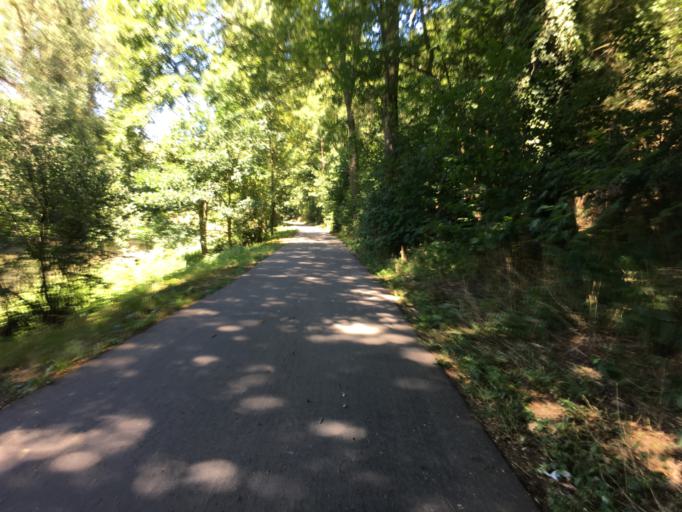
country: DE
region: Baden-Wuerttemberg
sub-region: Karlsruhe Region
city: Illingen
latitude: 48.9414
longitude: 8.9046
